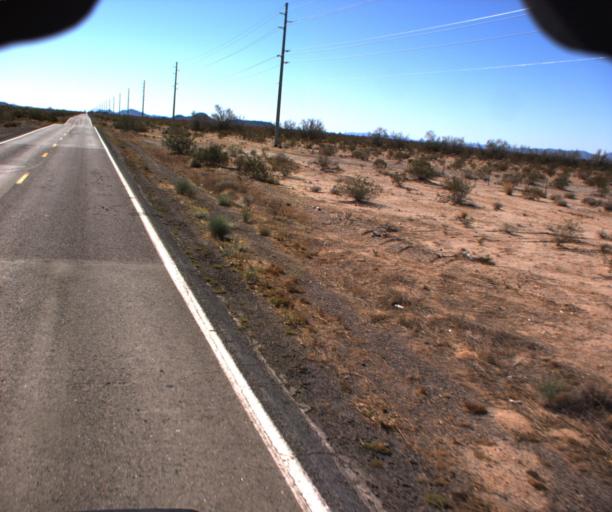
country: US
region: Arizona
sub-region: La Paz County
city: Salome
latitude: 33.8214
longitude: -113.8632
